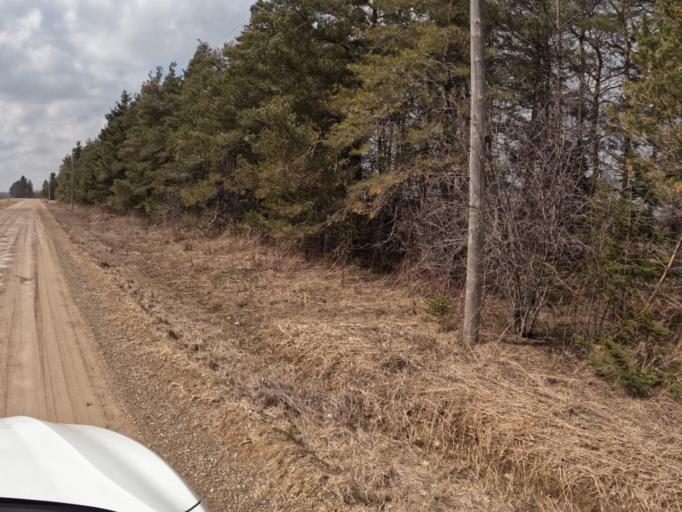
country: CA
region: Ontario
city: Shelburne
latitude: 44.0238
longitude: -80.2828
